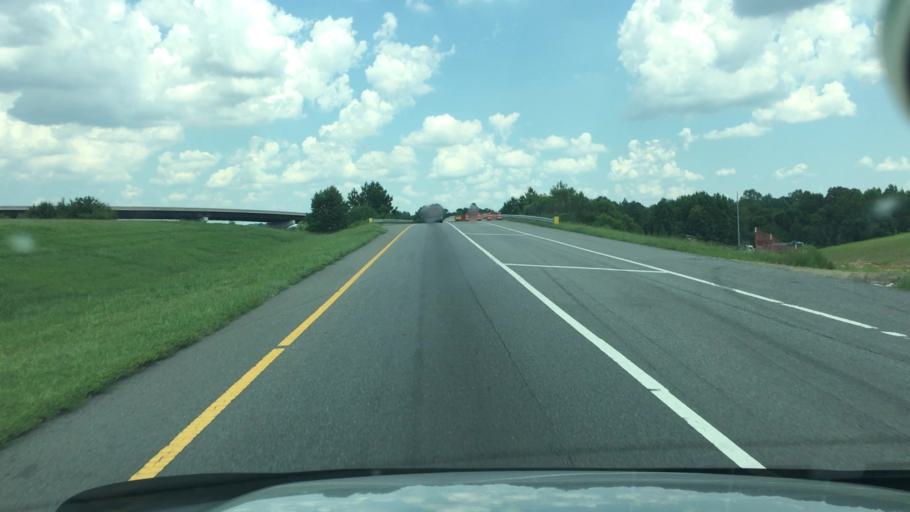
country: US
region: North Carolina
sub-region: Mecklenburg County
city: Huntersville
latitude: 35.3626
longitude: -80.8445
